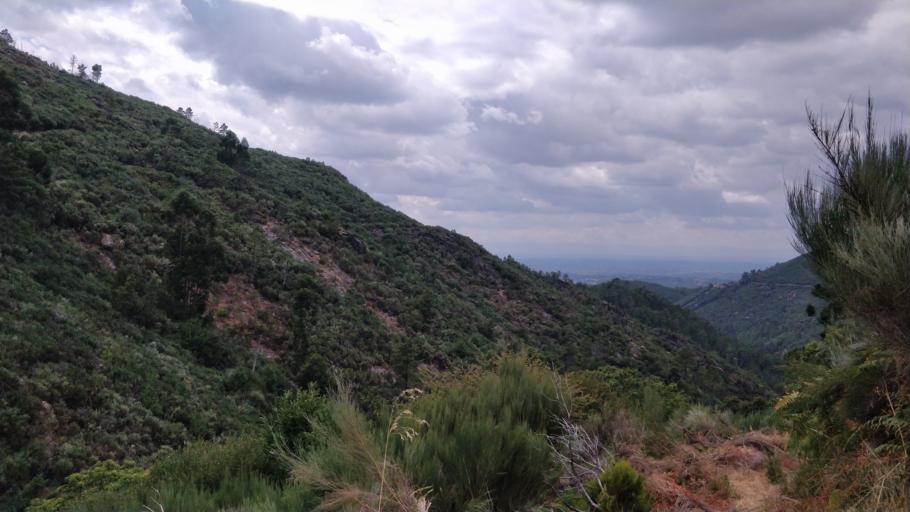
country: PT
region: Guarda
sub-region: Seia
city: Seia
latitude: 40.3791
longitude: -7.6877
